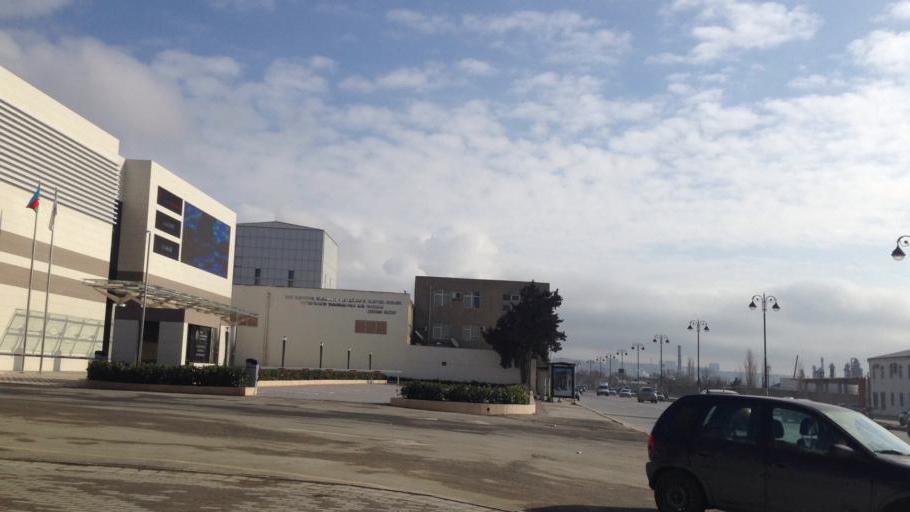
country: AZ
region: Baki
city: Baku
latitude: 40.3780
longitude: 49.8966
